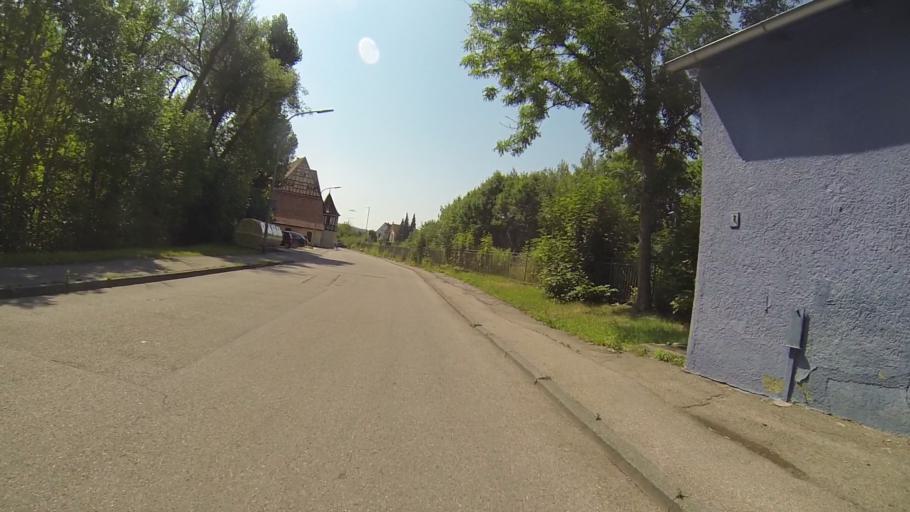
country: DE
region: Baden-Wuerttemberg
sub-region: Regierungsbezirk Stuttgart
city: Heidenheim an der Brenz
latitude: 48.7081
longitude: 10.1592
